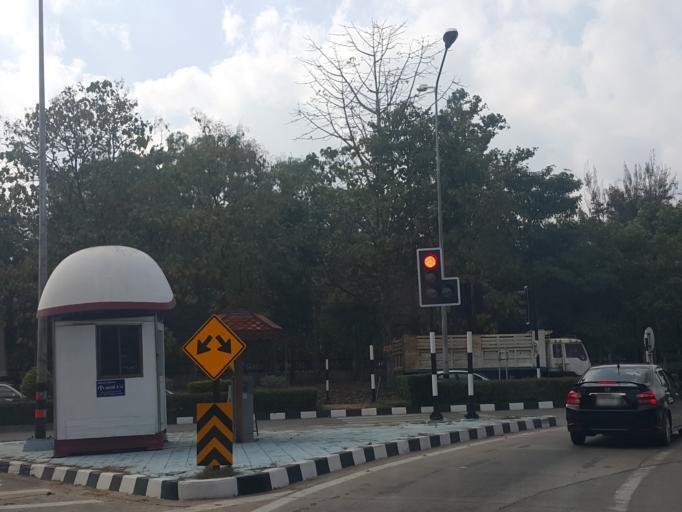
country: TH
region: Chiang Mai
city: Chiang Mai
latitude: 18.8396
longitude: 98.9743
